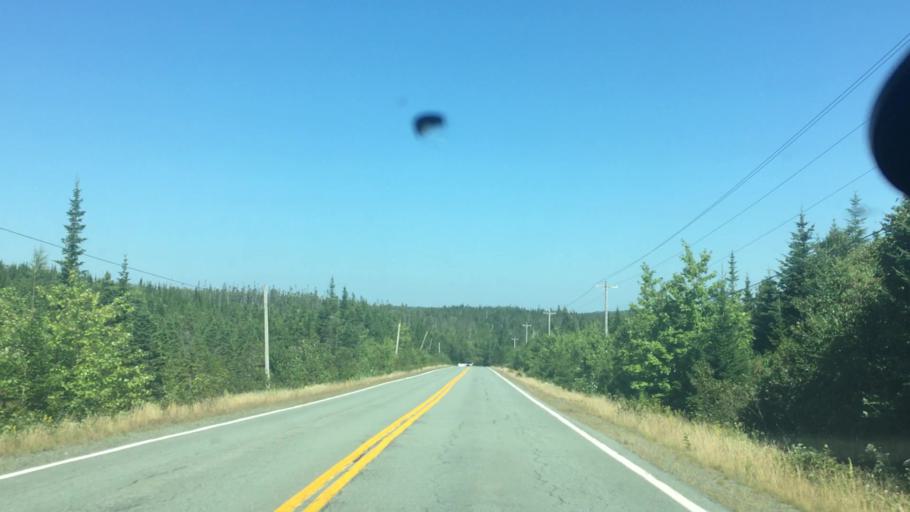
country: CA
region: Nova Scotia
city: Antigonish
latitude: 45.0102
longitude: -62.1055
